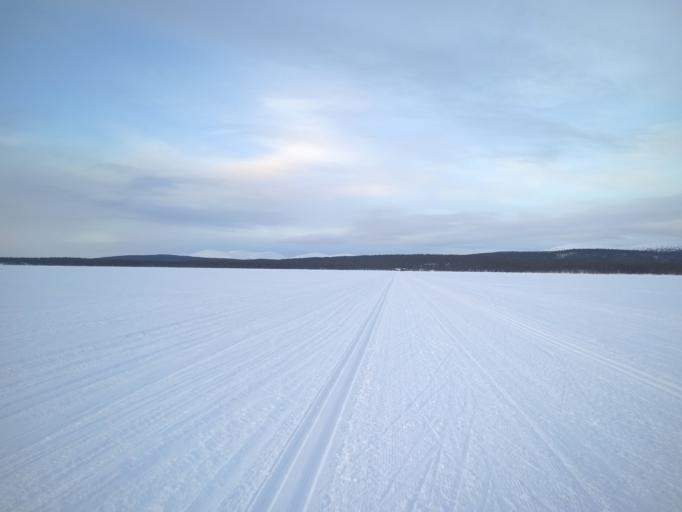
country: FI
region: Lapland
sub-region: Tunturi-Lappi
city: Muonio
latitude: 67.9294
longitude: 24.0246
